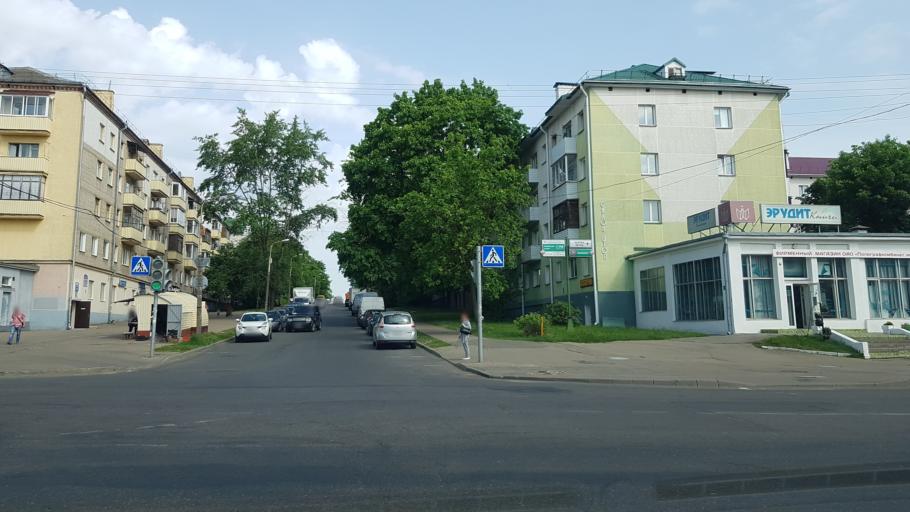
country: BY
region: Minsk
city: Minsk
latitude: 53.8941
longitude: 27.5216
